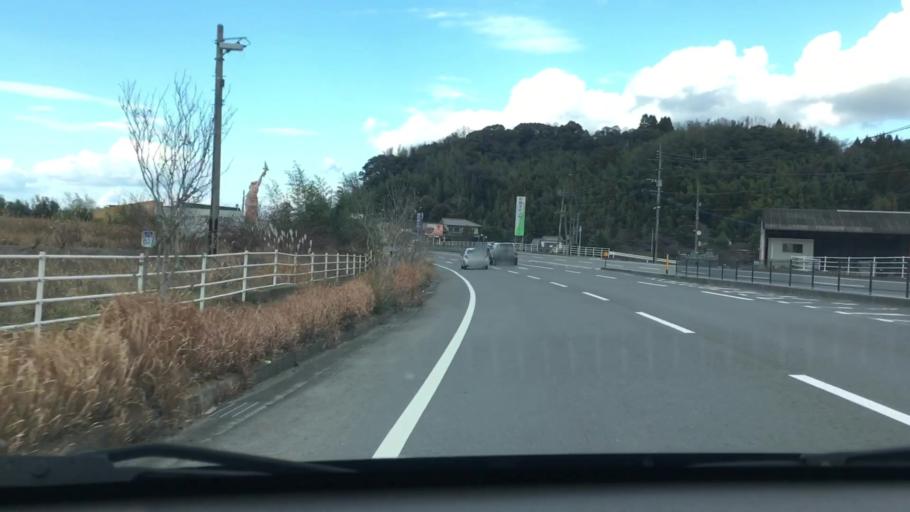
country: JP
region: Oita
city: Oita
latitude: 33.1339
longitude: 131.6601
